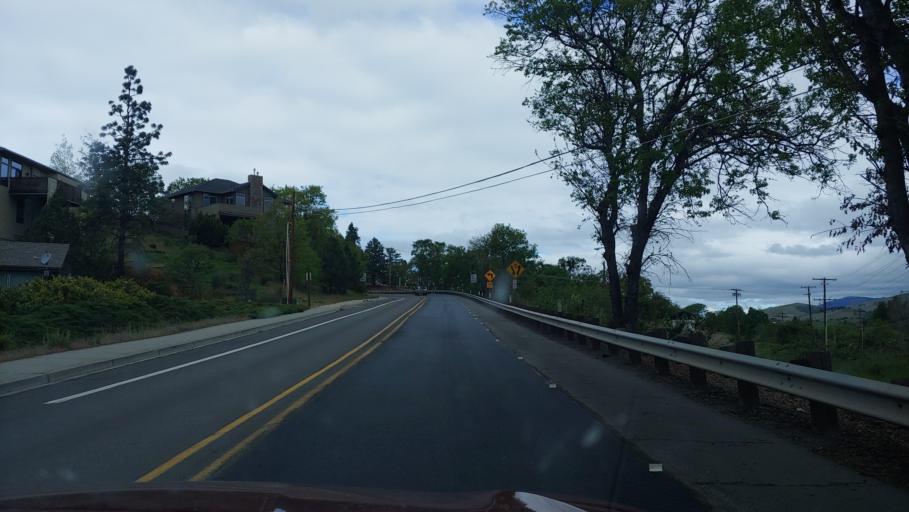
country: US
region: Oregon
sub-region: Jackson County
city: Ashland
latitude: 42.1854
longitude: -122.6589
